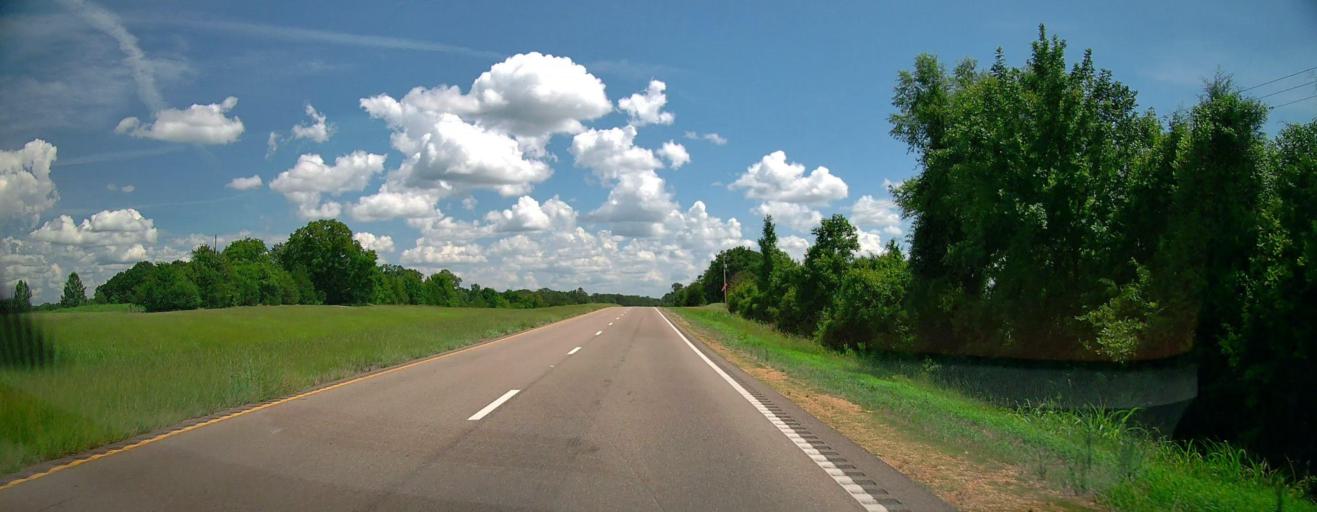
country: US
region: Mississippi
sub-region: Monroe County
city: Amory
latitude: 33.9507
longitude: -88.6034
